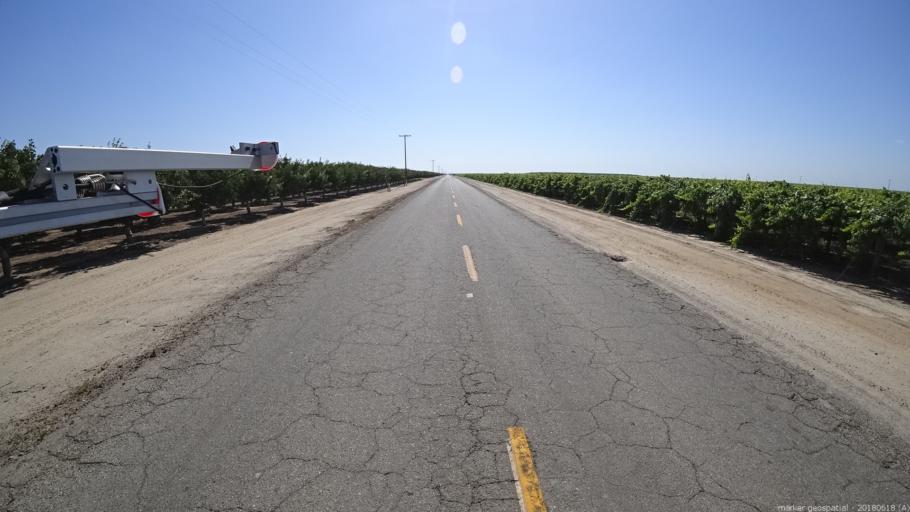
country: US
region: California
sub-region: Fresno County
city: Mendota
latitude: 36.8366
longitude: -120.2526
